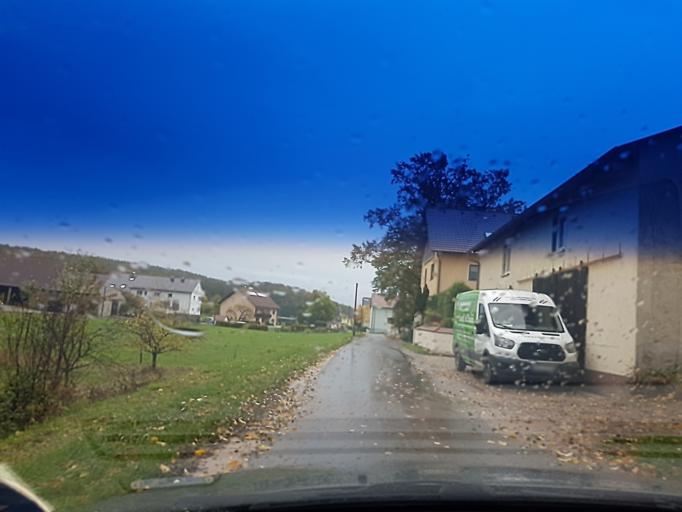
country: DE
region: Bavaria
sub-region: Regierungsbezirk Mittelfranken
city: Wachenroth
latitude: 49.7593
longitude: 10.6888
